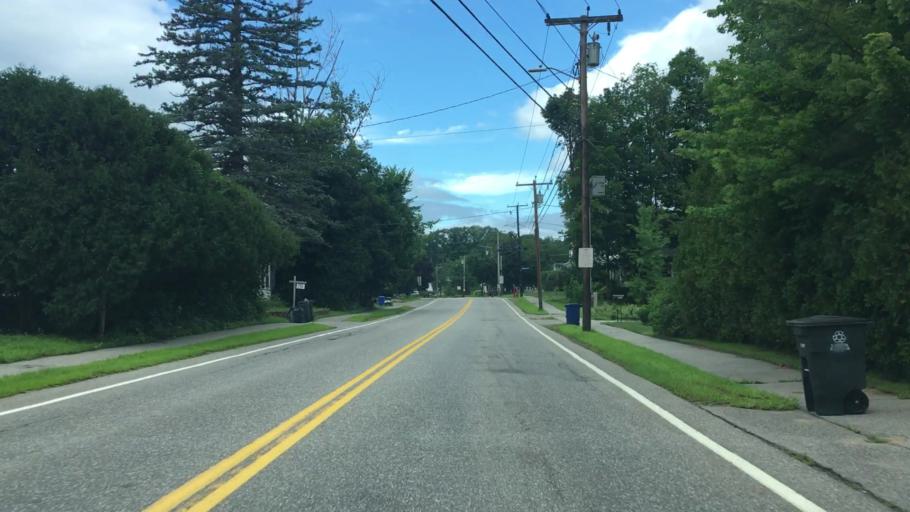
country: US
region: New Hampshire
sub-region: Belknap County
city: Laconia
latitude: 43.5556
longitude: -71.4697
